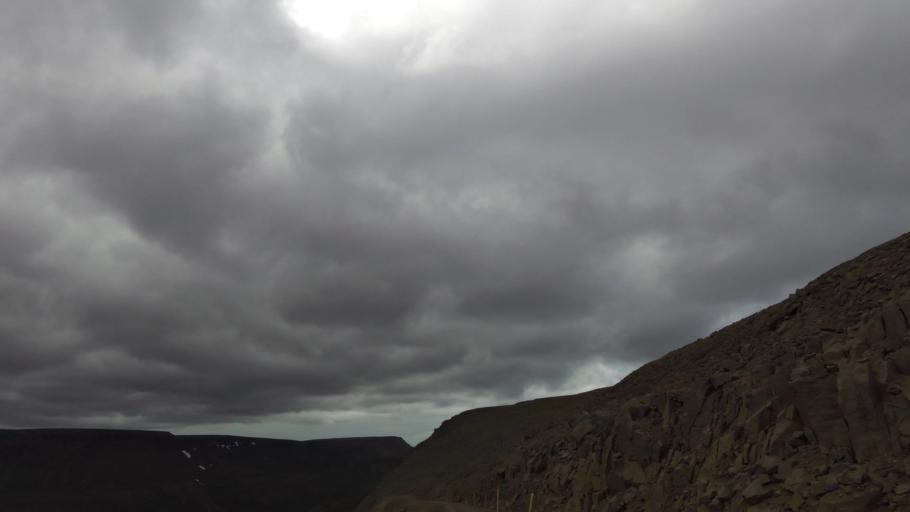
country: IS
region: Westfjords
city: Isafjoerdur
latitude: 66.1783
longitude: -23.3635
